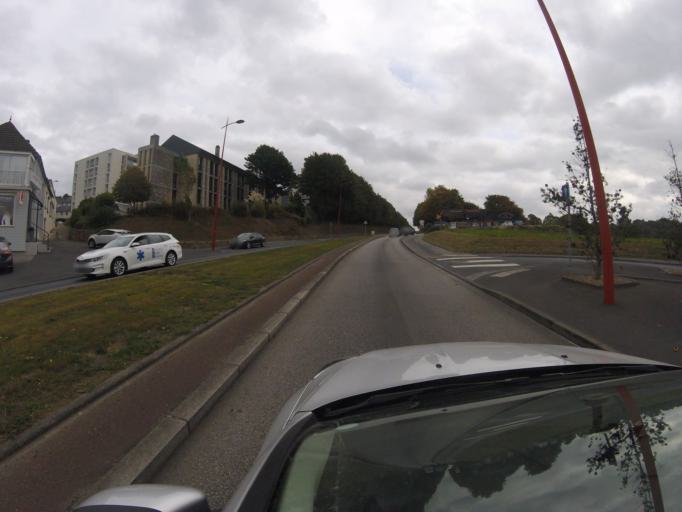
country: FR
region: Lower Normandy
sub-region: Departement de la Manche
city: Cherbourg-Octeville
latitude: 49.6193
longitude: -1.6121
